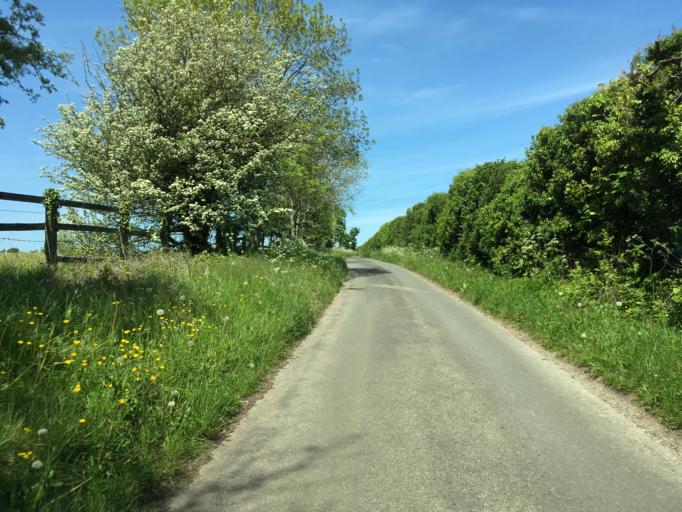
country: GB
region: England
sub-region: Gloucestershire
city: Brimscombe
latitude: 51.7265
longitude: -2.1848
